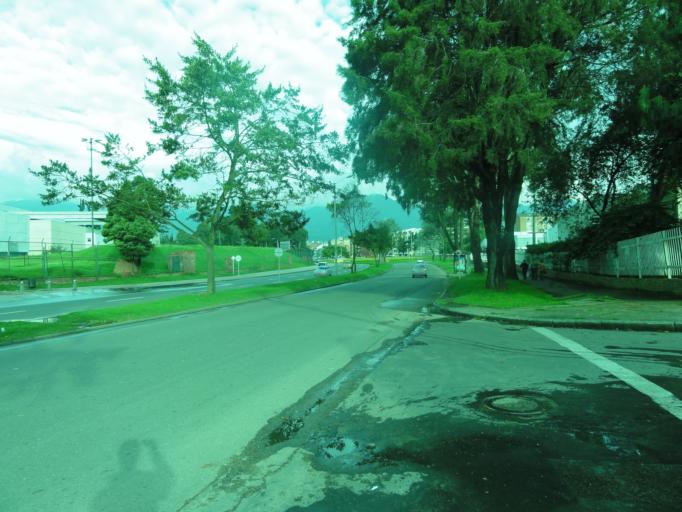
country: CO
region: Bogota D.C.
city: Bogota
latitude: 4.6547
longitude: -74.0854
